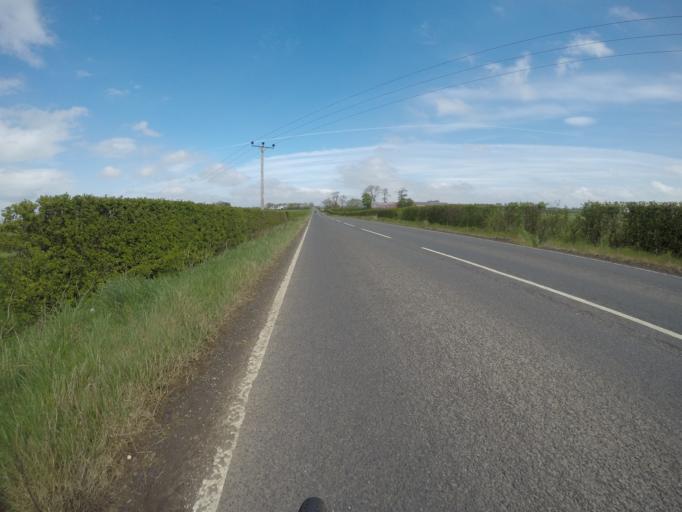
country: GB
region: Scotland
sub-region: East Ayrshire
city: Kilmaurs
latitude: 55.6587
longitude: -4.5531
